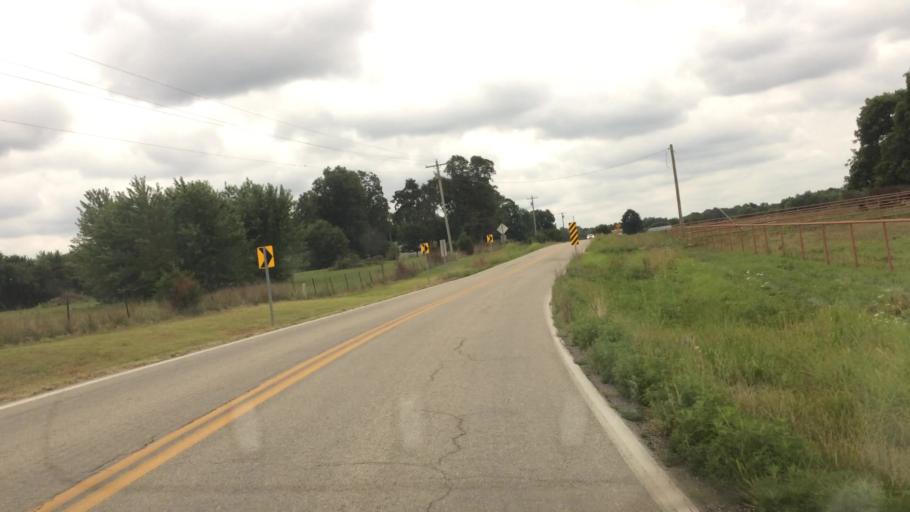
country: US
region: Missouri
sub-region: Greene County
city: Strafford
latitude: 37.2991
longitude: -93.1215
